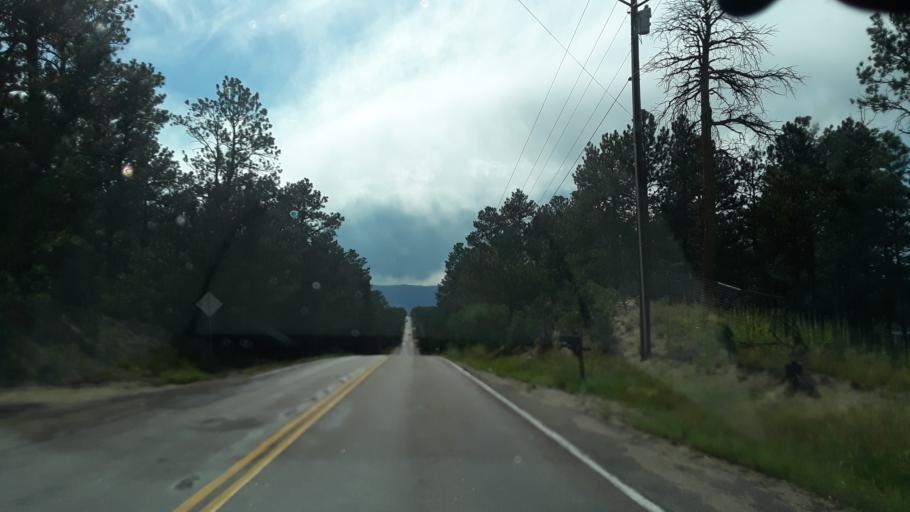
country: US
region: Colorado
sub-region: El Paso County
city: Black Forest
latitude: 39.0128
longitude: -104.7095
